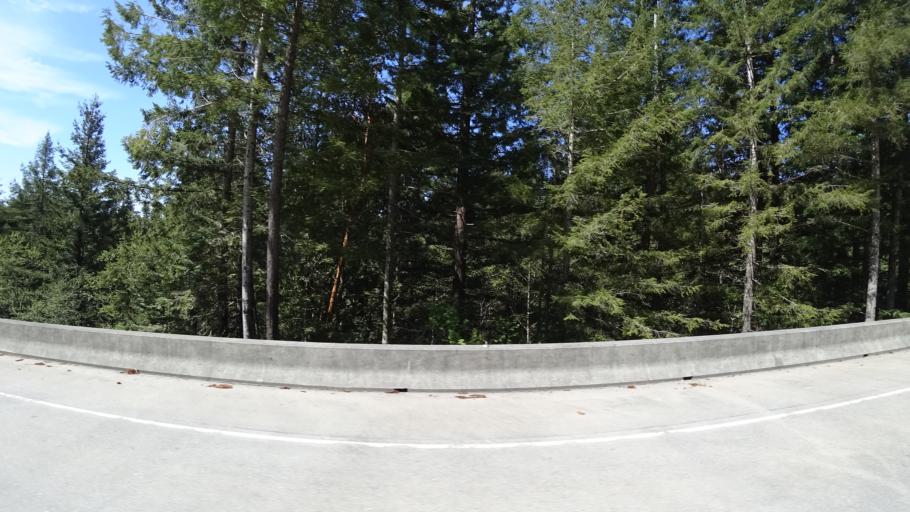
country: US
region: California
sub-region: Humboldt County
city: Westhaven-Moonstone
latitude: 41.3721
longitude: -123.9909
